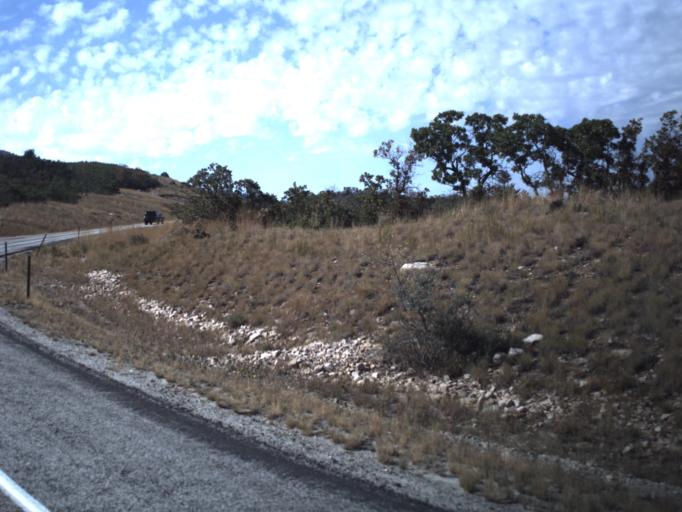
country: US
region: Utah
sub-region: Morgan County
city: Mountain Green
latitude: 41.2088
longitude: -111.8390
